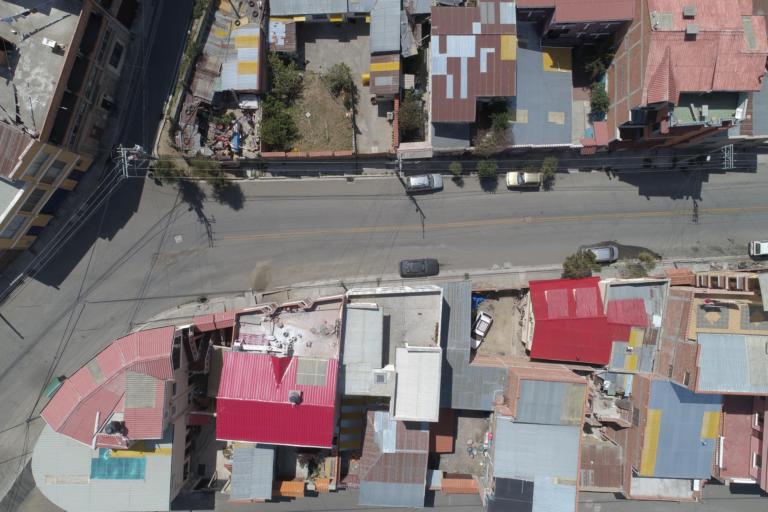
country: BO
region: La Paz
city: La Paz
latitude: -16.4979
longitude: -68.1013
